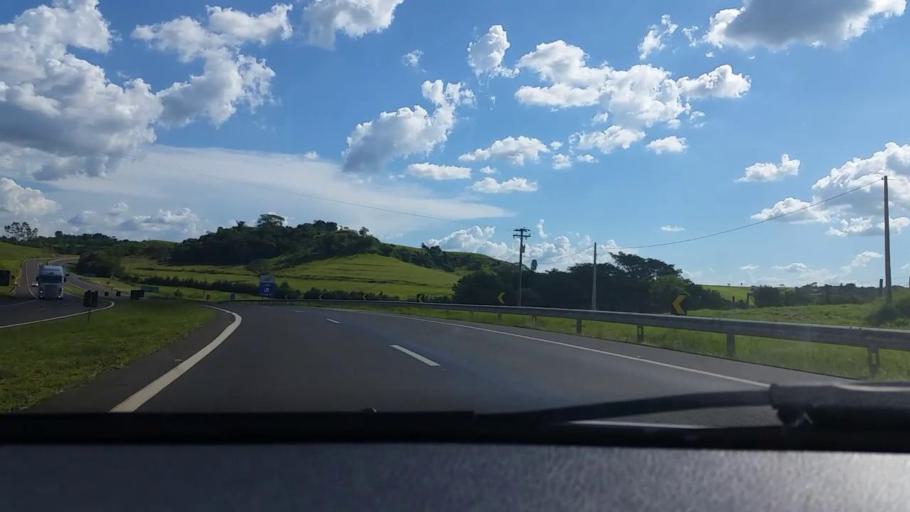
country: BR
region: Sao Paulo
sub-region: Bauru
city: Bauru
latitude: -22.4279
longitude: -49.1313
